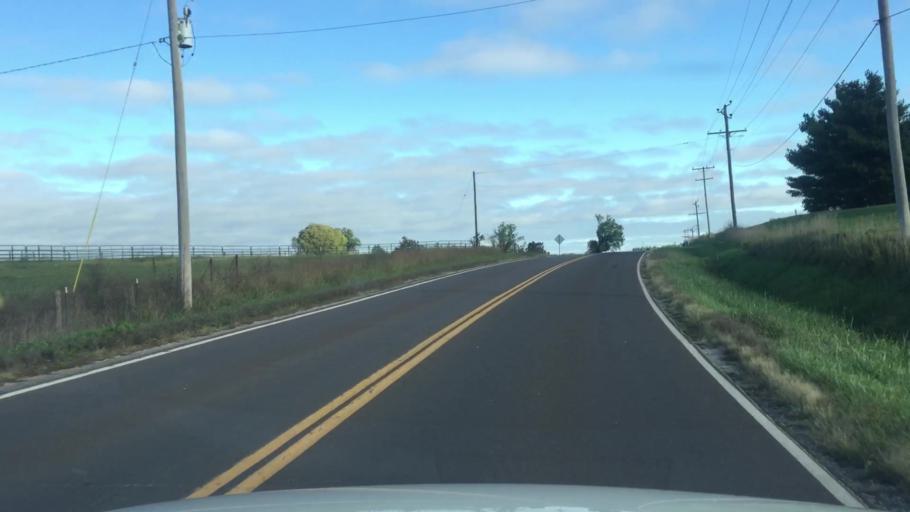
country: US
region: Missouri
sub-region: Howard County
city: New Franklin
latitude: 39.0261
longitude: -92.7471
